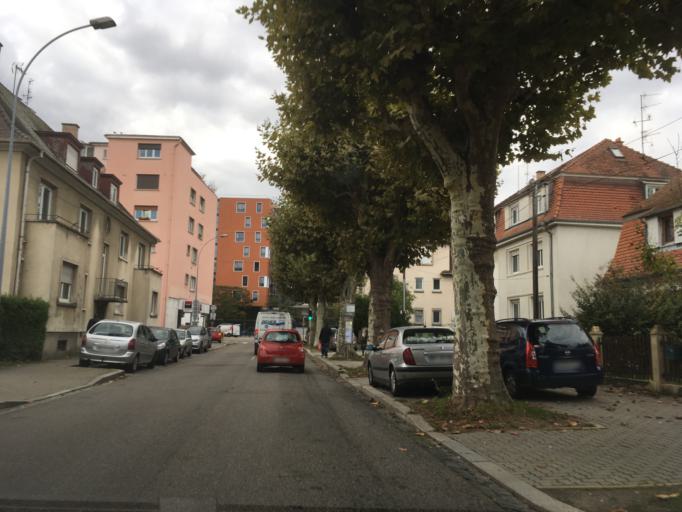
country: FR
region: Alsace
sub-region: Departement du Bas-Rhin
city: Strasbourg
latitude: 48.5535
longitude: 7.7458
